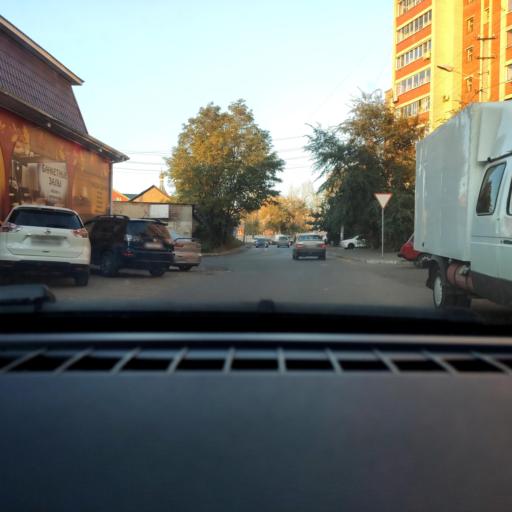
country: RU
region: Voronezj
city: Voronezh
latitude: 51.6981
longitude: 39.2666
